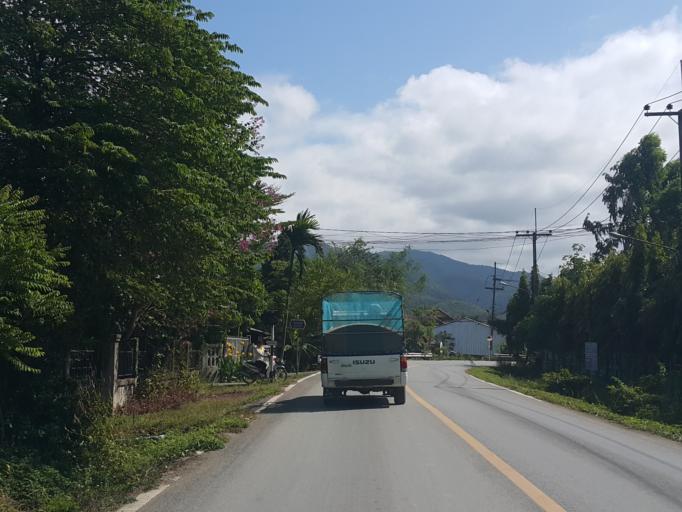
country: TH
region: Chiang Mai
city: San Kamphaeng
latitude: 18.6916
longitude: 99.1581
